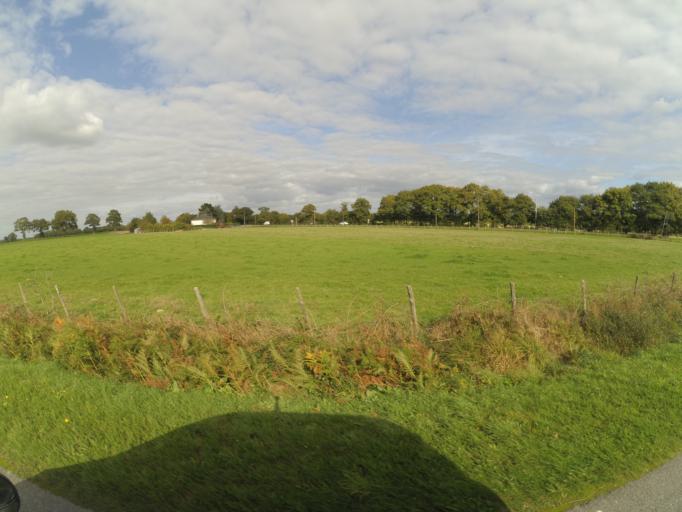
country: FR
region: Pays de la Loire
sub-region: Departement de la Loire-Atlantique
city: Plesse
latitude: 47.5160
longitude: -1.8875
